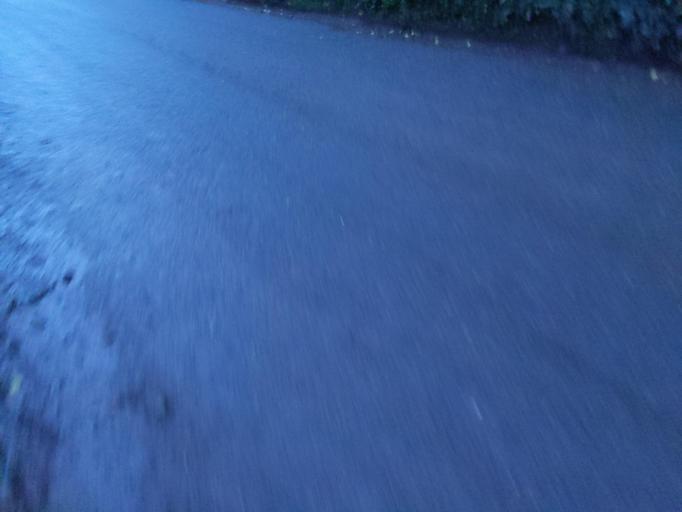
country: GB
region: England
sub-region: Devon
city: Yealmpton
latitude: 50.3376
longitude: -4.0140
